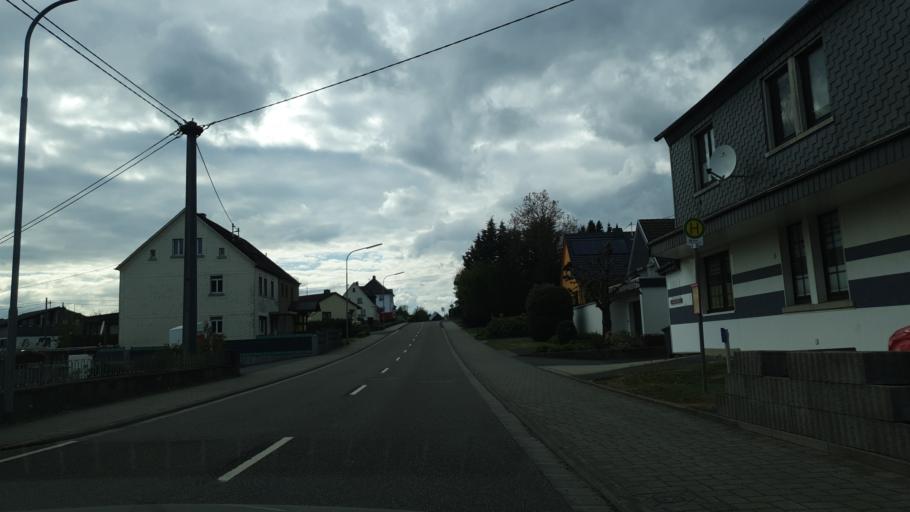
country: DE
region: Rheinland-Pfalz
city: Hohn
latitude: 50.6209
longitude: 7.9758
